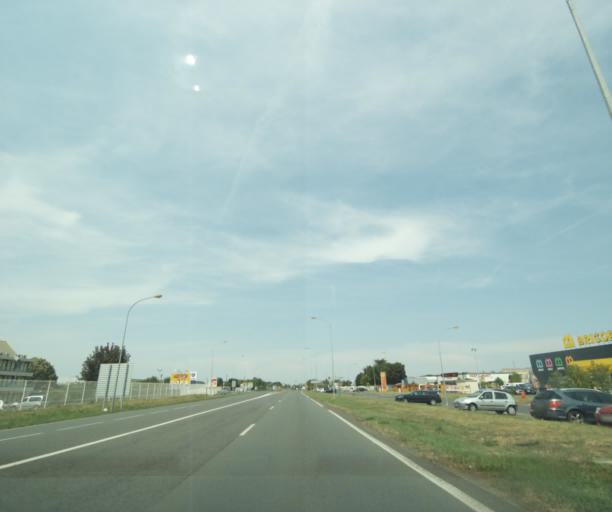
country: FR
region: Poitou-Charentes
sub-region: Departement de la Vienne
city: Antran
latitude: 46.8419
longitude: 0.5488
